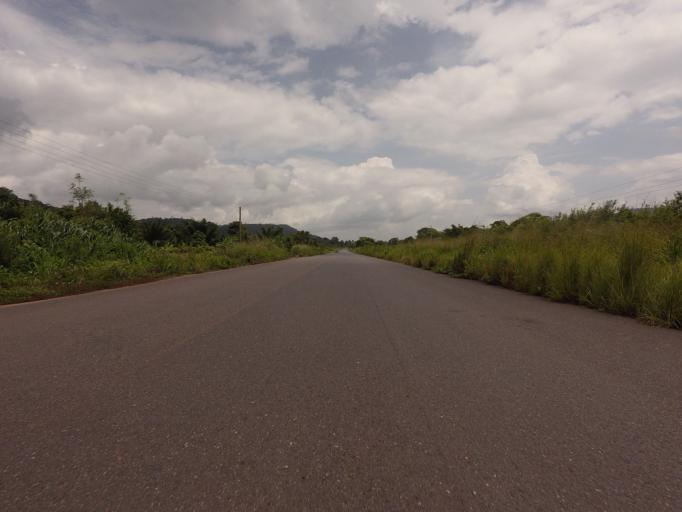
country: GH
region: Volta
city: Ho
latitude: 6.5512
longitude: 0.2559
